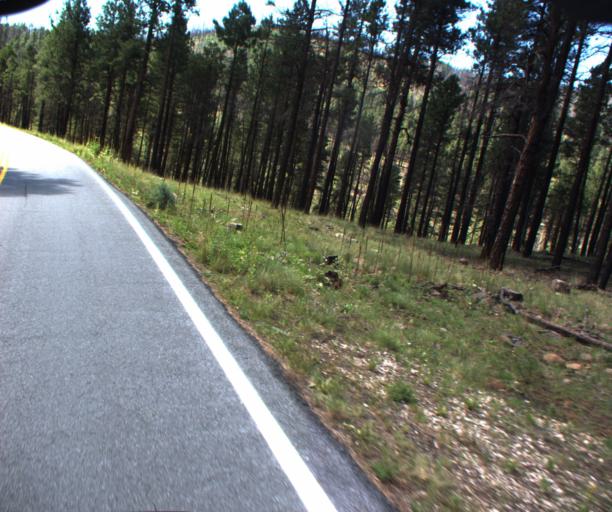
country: US
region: Arizona
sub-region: Apache County
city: Eagar
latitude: 33.7523
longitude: -109.2163
